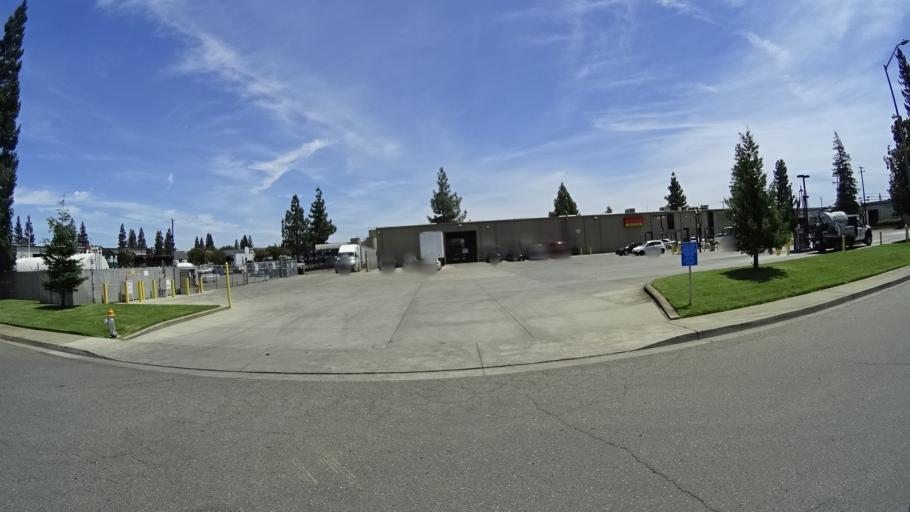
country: US
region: California
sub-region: Sacramento County
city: Florin
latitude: 38.5363
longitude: -121.4044
